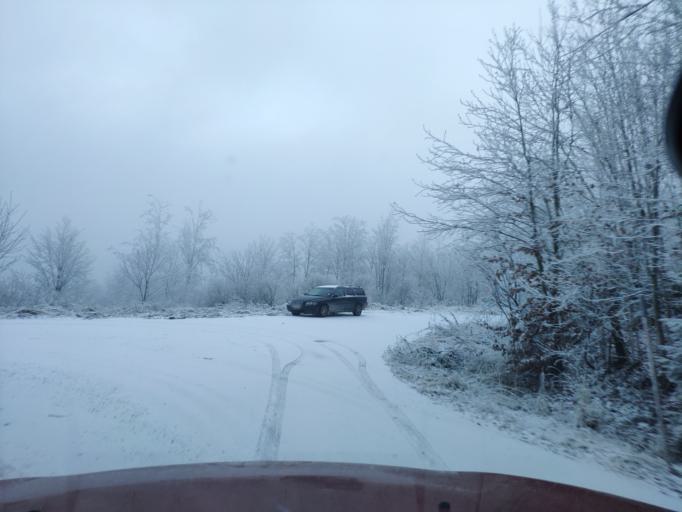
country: SK
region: Kosicky
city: Dobsina
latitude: 48.8116
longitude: 20.4846
